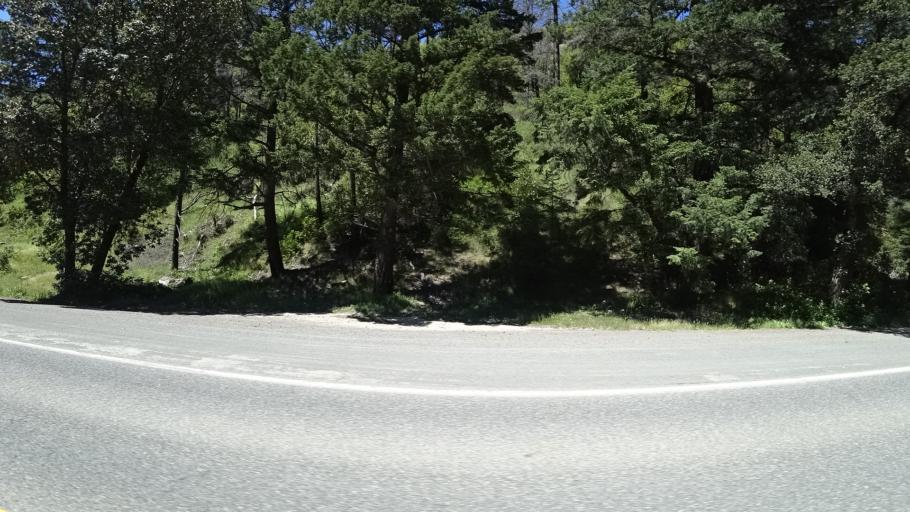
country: US
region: California
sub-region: Trinity County
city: Hayfork
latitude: 40.7745
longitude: -123.3276
